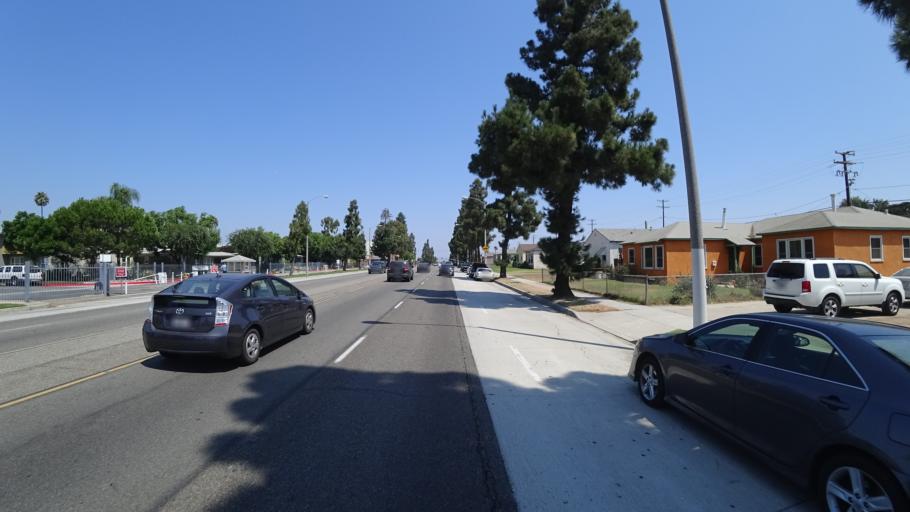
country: US
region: California
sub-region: Los Angeles County
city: Westmont
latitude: 33.9538
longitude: -118.3264
